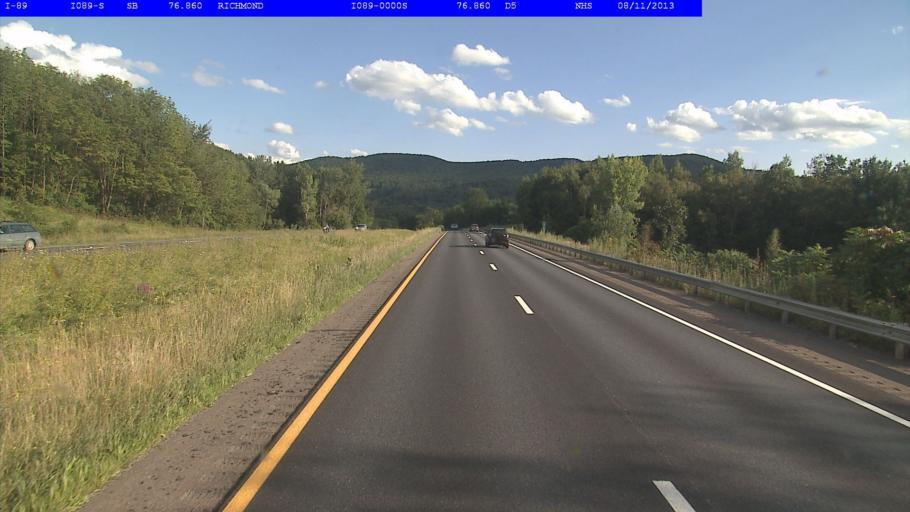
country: US
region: Vermont
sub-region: Chittenden County
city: Williston
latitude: 44.4084
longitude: -72.9904
